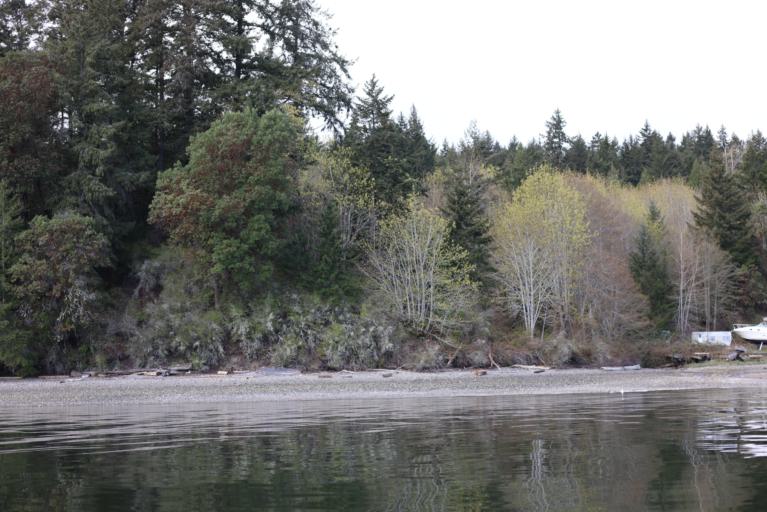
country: CA
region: British Columbia
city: North Saanich
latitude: 48.6018
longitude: -123.5202
